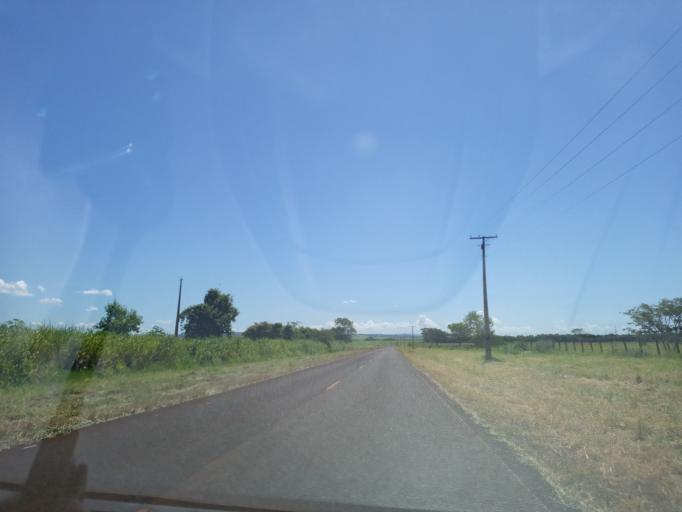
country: BR
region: Goias
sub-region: Itumbiara
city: Itumbiara
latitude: -18.4110
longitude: -49.1282
